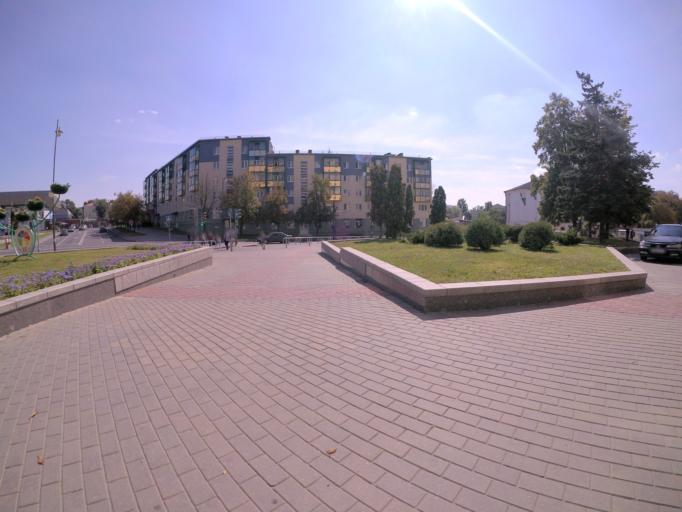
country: BY
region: Grodnenskaya
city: Hrodna
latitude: 53.6866
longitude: 23.8459
